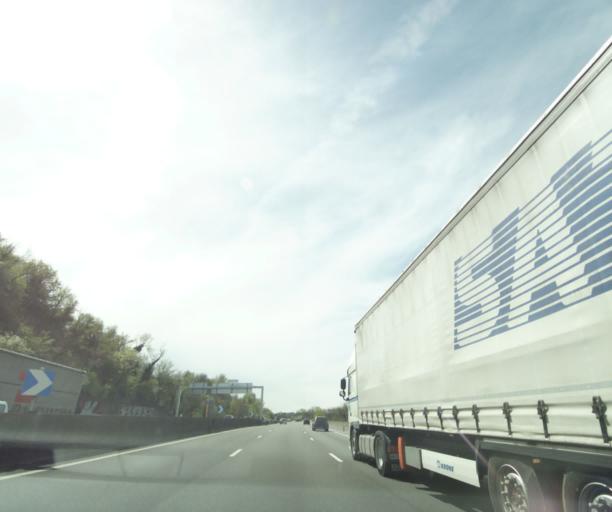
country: FR
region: Rhone-Alpes
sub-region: Departement du Rhone
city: Saint-Cyr-sur-le-Rhone
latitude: 45.4959
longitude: 4.8377
